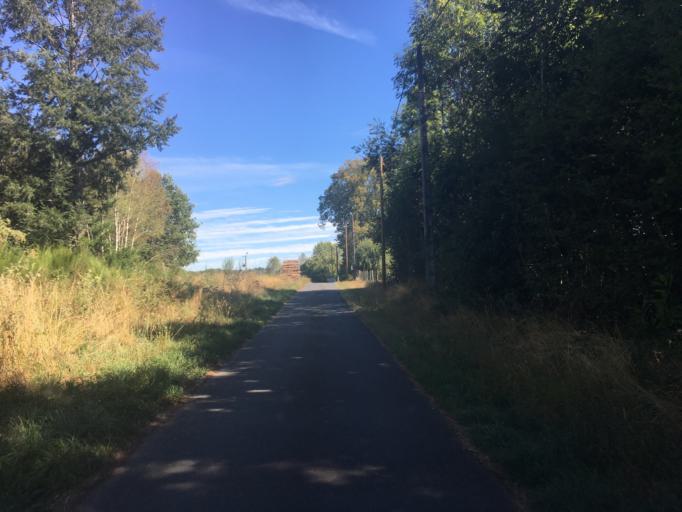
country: FR
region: Limousin
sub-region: Departement de la Correze
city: Meymac
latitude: 45.4263
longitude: 2.1579
